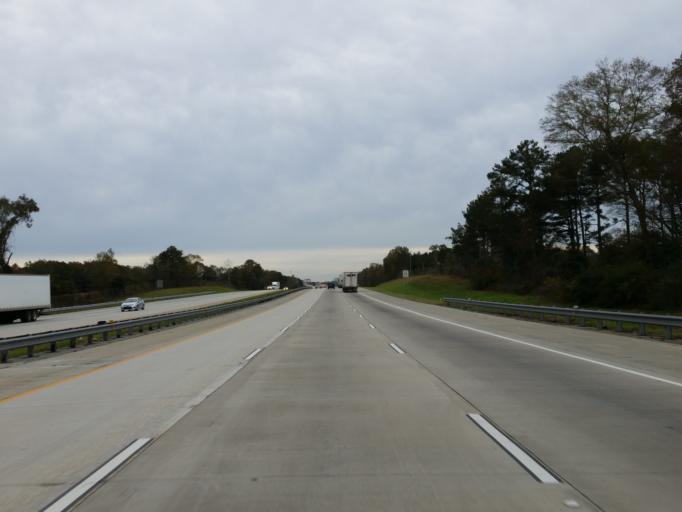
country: US
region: Georgia
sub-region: Dooly County
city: Unadilla
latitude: 32.2766
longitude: -83.7548
